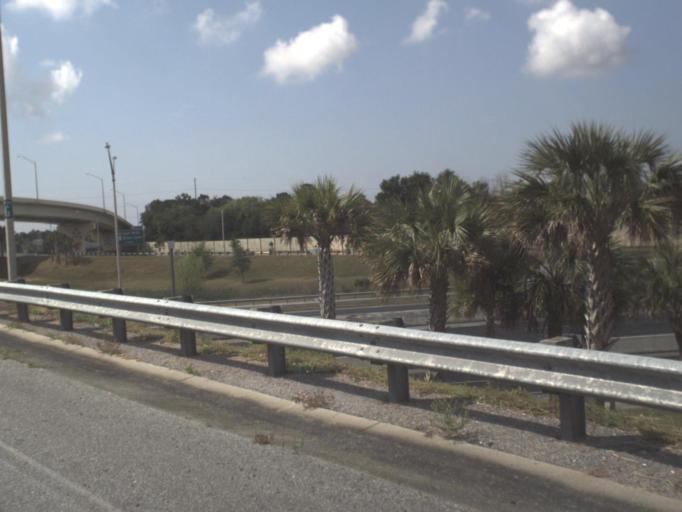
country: US
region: Florida
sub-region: Escambia County
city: Ferry Pass
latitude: 30.5042
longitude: -87.2309
